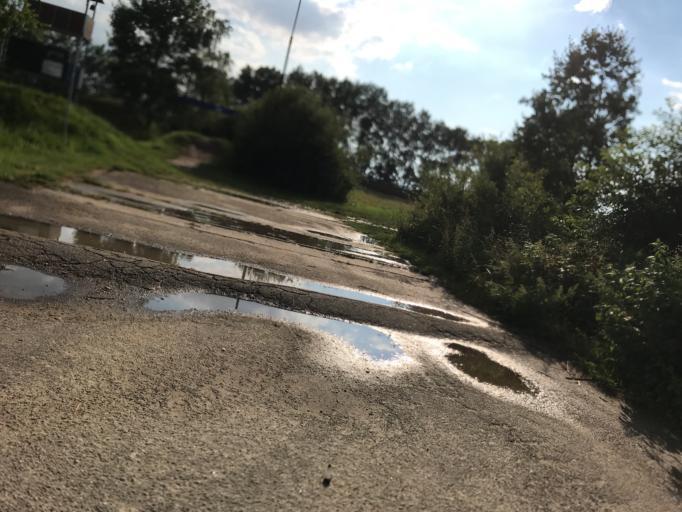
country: CZ
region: Jihocesky
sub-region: Okres Jindrichuv Hradec
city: Trebon
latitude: 49.0225
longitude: 14.7582
